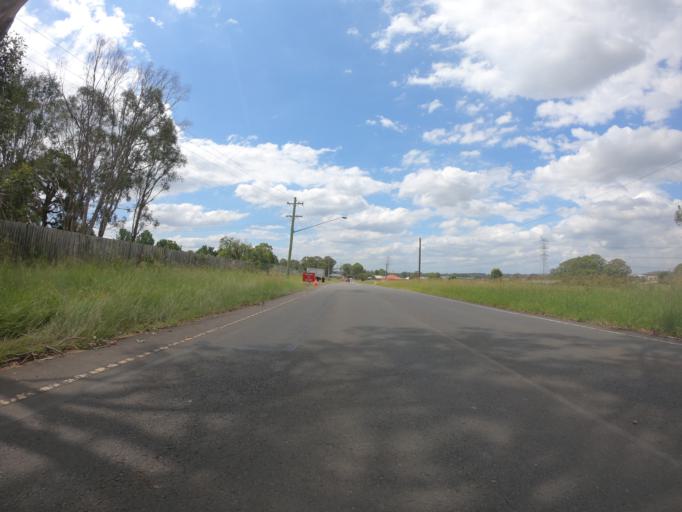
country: AU
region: New South Wales
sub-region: Penrith Municipality
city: Kingswood Park
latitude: -33.8257
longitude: 150.7601
